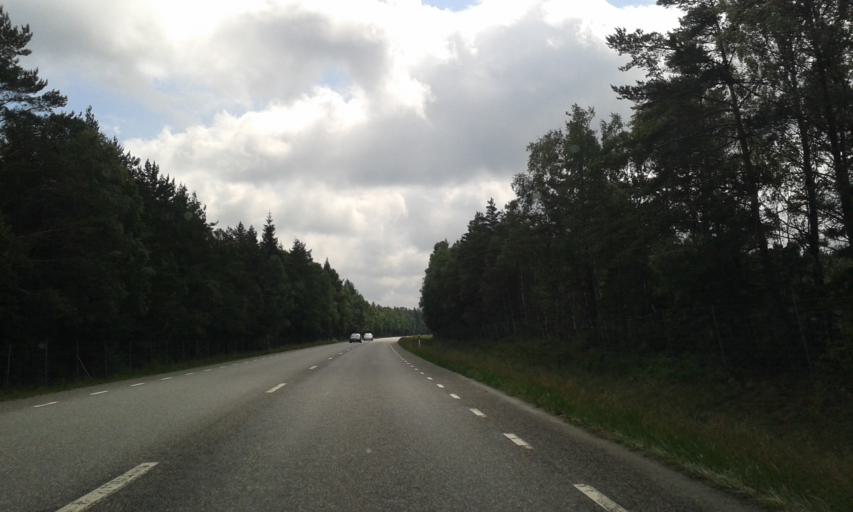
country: SE
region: Vaestra Goetaland
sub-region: Tranemo Kommun
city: Limmared
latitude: 57.5515
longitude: 13.3156
